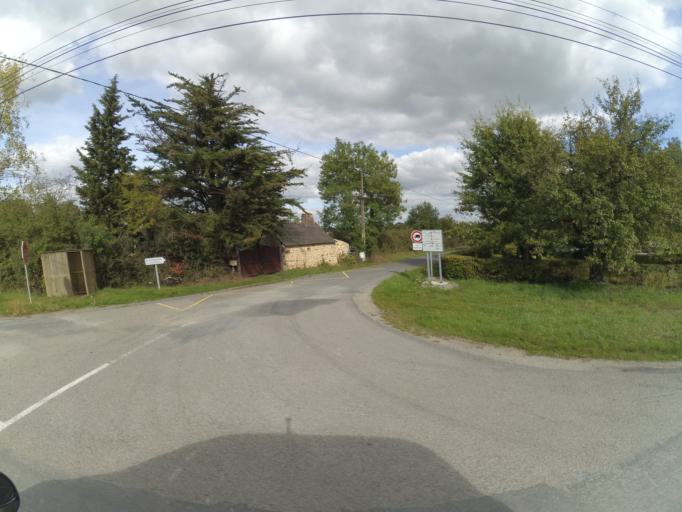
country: FR
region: Pays de la Loire
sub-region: Departement de la Loire-Atlantique
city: Casson
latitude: 47.3984
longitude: -1.5684
